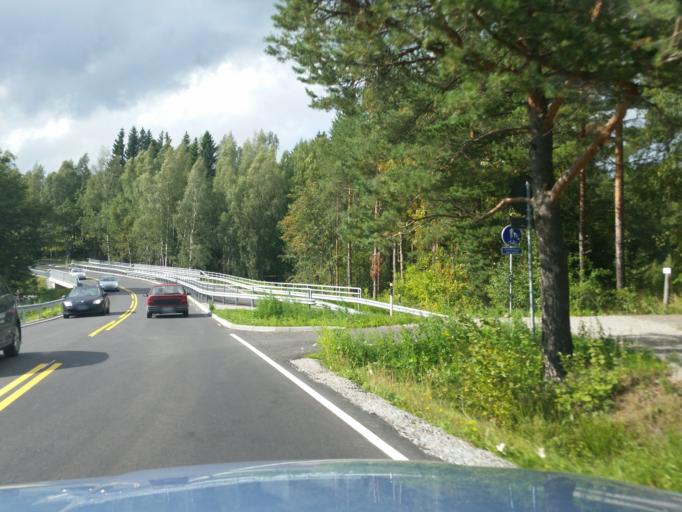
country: FI
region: Varsinais-Suomi
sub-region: Aboland-Turunmaa
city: Laensi-Turunmaa
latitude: 60.2467
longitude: 22.2324
